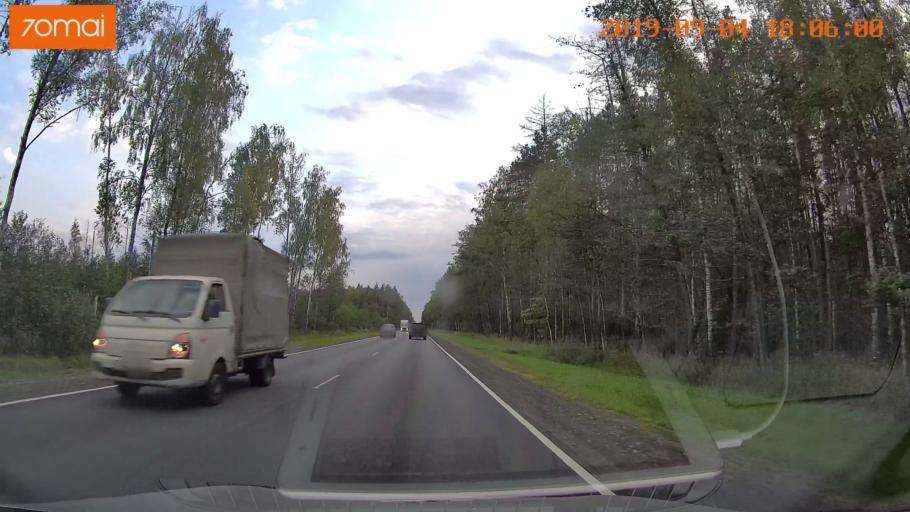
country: RU
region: Moskovskaya
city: Il'inskiy Pogost
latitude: 55.4354
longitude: 38.8197
